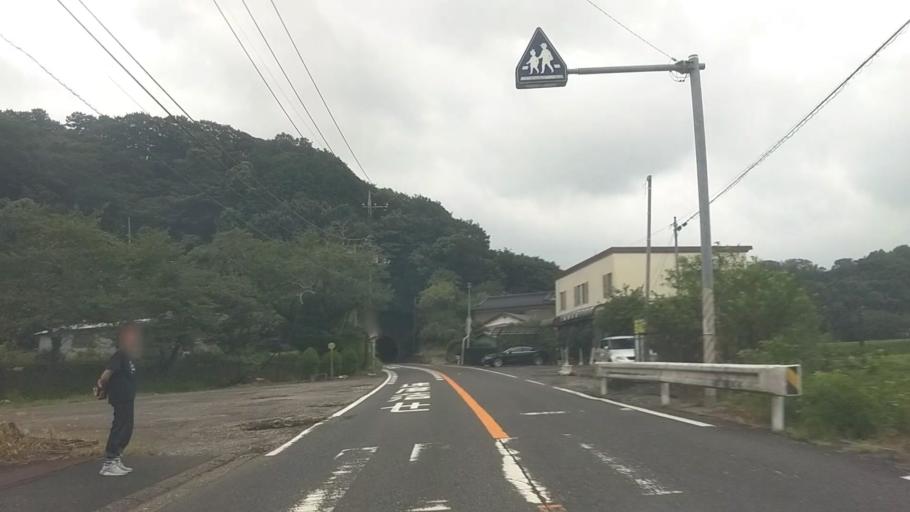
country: JP
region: Chiba
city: Kawaguchi
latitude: 35.2580
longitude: 140.0644
